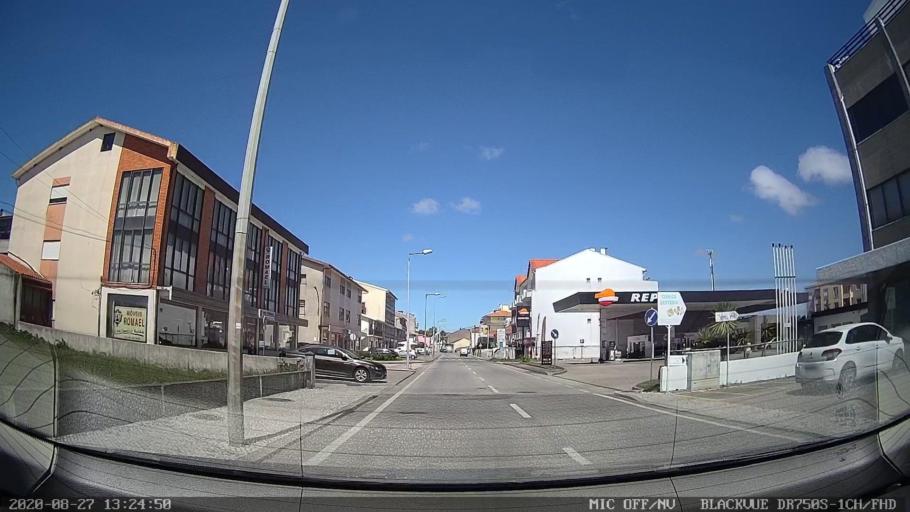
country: PT
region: Aveiro
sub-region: Vagos
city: Vagos
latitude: 40.5509
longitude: -8.6800
